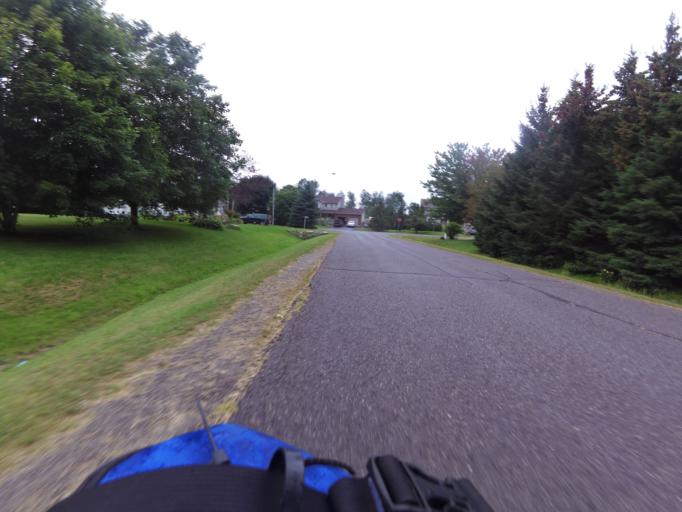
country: CA
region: Ontario
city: Ottawa
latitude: 45.2294
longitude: -75.4812
